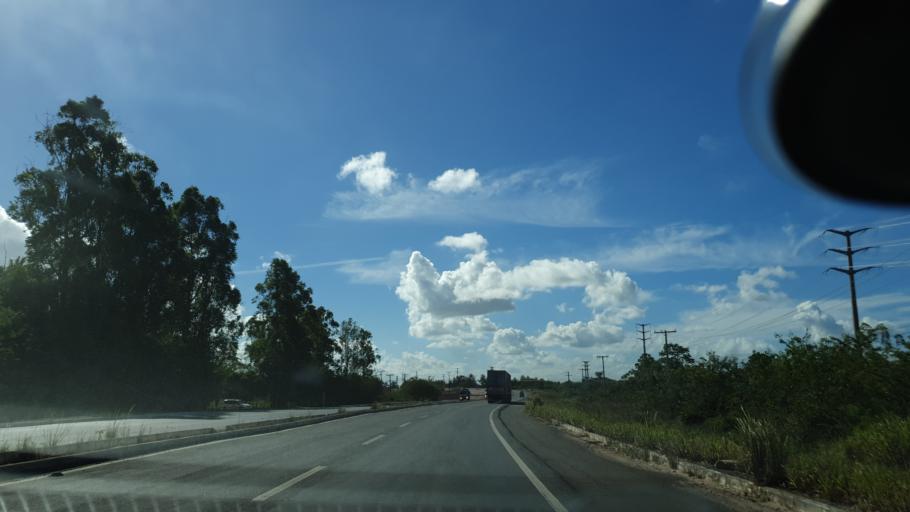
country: BR
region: Bahia
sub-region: Camacari
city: Camacari
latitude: -12.6848
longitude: -38.2615
